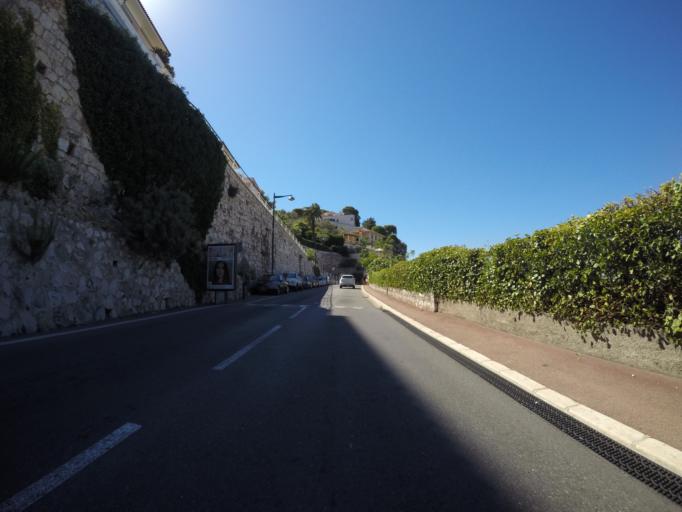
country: FR
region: Provence-Alpes-Cote d'Azur
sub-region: Departement des Alpes-Maritimes
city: Beaulieu-sur-Mer
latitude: 43.7004
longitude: 7.3265
